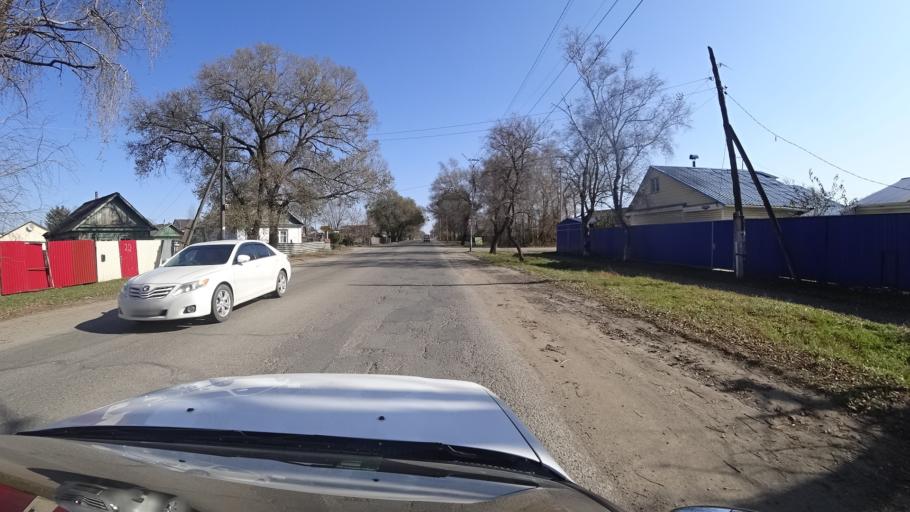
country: RU
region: Primorskiy
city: Dal'nerechensk
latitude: 45.9245
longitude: 133.7424
